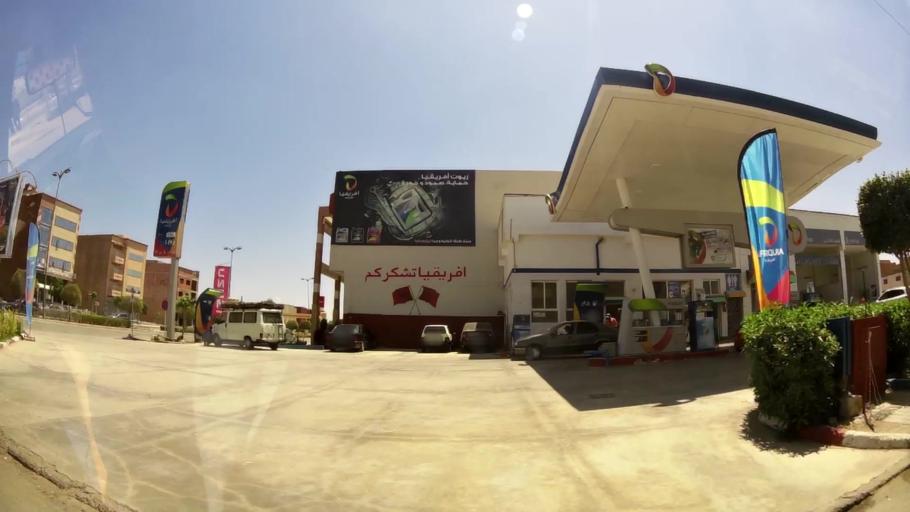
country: MA
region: Oriental
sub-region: Oujda-Angad
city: Oujda
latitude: 34.6838
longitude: -1.9513
